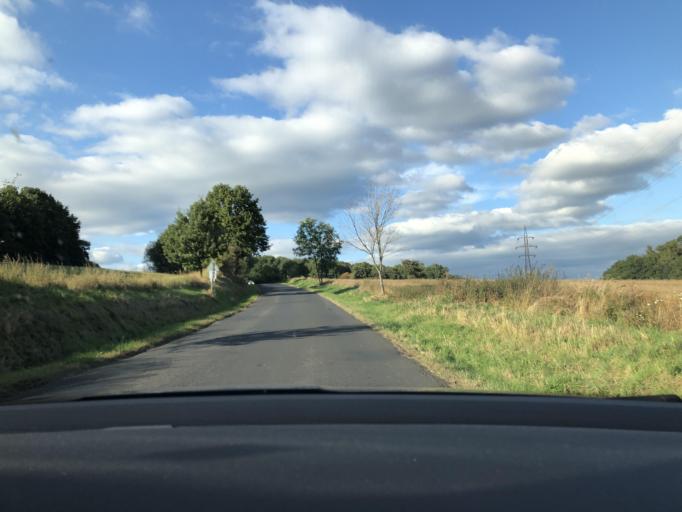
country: CZ
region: Ustecky
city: Zitenice
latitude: 50.5747
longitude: 14.1751
